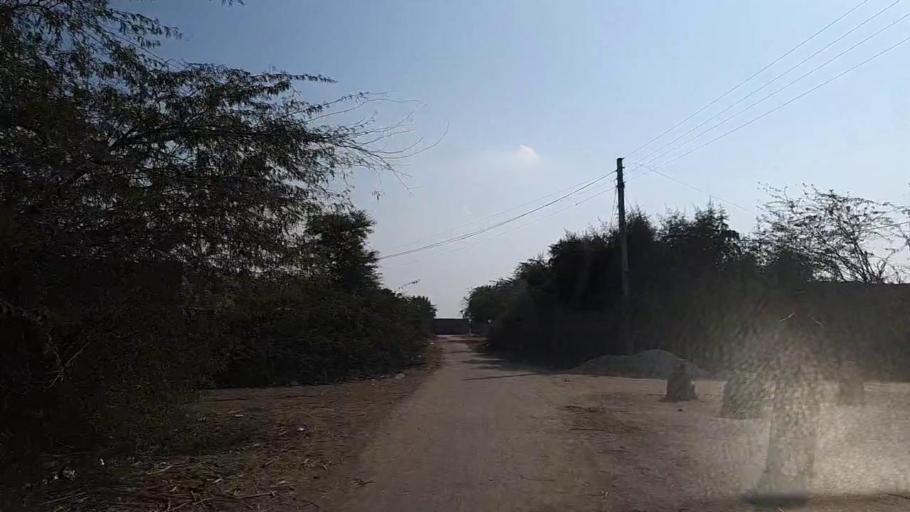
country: PK
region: Sindh
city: Jam Sahib
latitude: 26.2736
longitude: 68.5841
